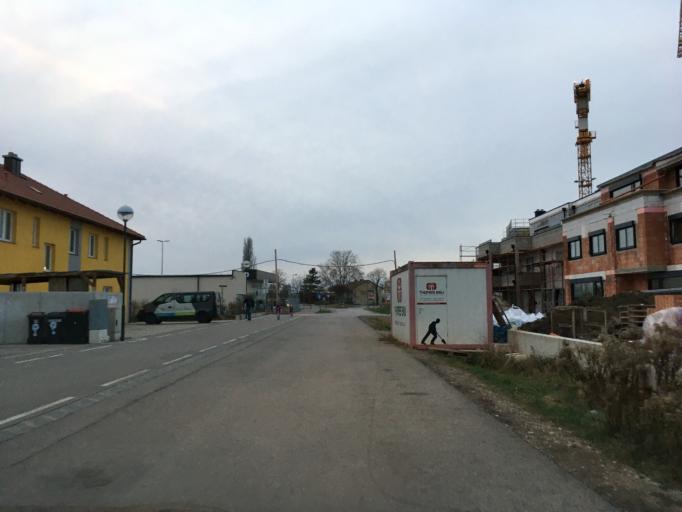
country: AT
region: Lower Austria
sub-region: Politischer Bezirk Tulln
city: Tulln
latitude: 48.3186
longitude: 16.0592
